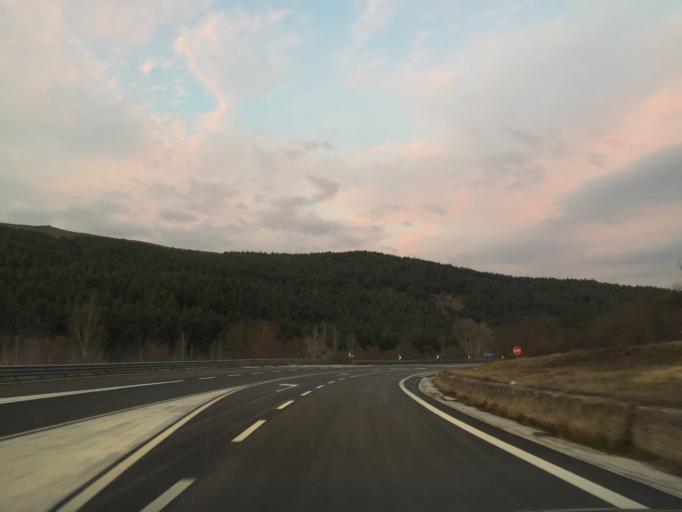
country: IT
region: Molise
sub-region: Provincia di Campobasso
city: Gambatesa
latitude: 41.5258
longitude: 14.9125
